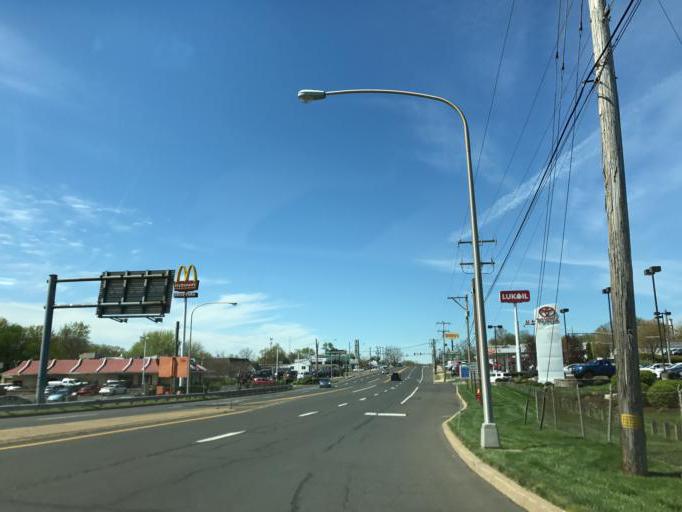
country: US
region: Pennsylvania
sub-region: Bucks County
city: Langhorne Manor
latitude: 40.1652
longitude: -74.9018
